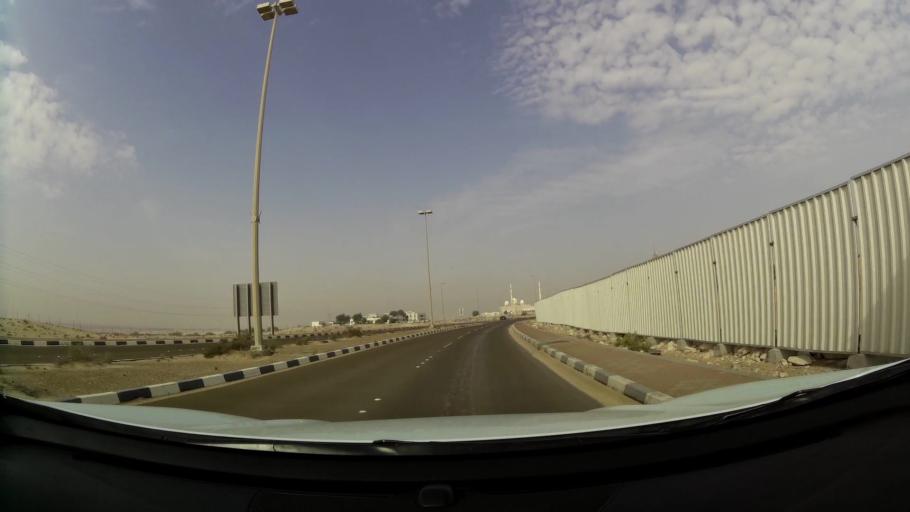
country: AE
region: Abu Dhabi
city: Abu Dhabi
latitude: 24.2559
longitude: 54.7089
